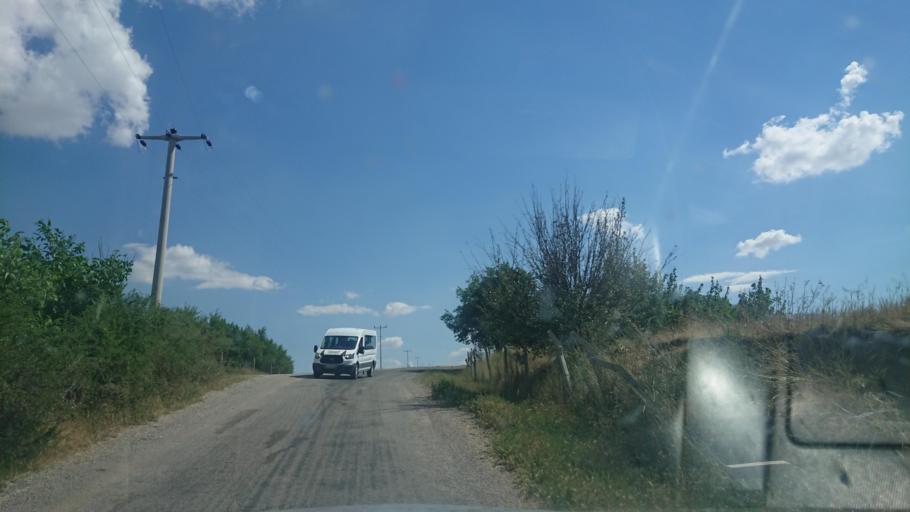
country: TR
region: Aksaray
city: Agacoren
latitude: 38.7662
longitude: 33.7841
